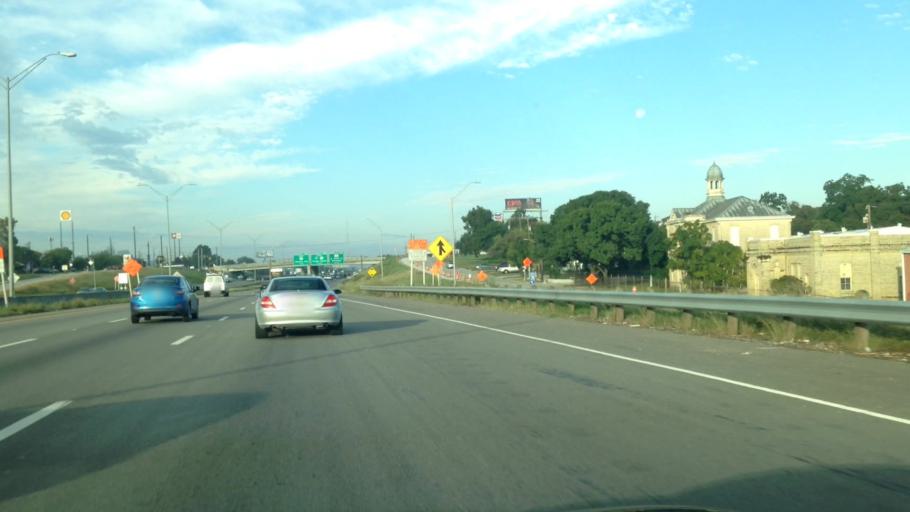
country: US
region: Texas
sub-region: Bexar County
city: Terrell Hills
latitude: 29.4393
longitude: -98.4567
